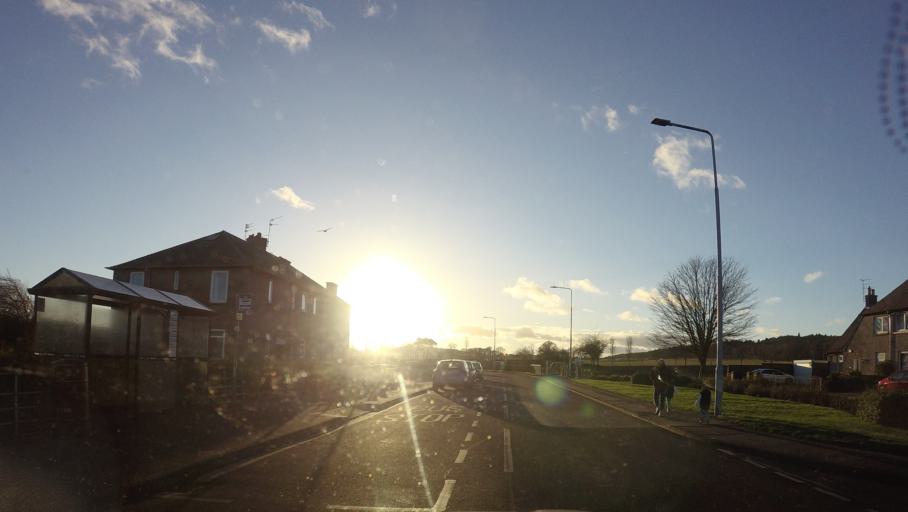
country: GB
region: Scotland
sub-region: Fife
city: Tayport
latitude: 56.4435
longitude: -2.8832
